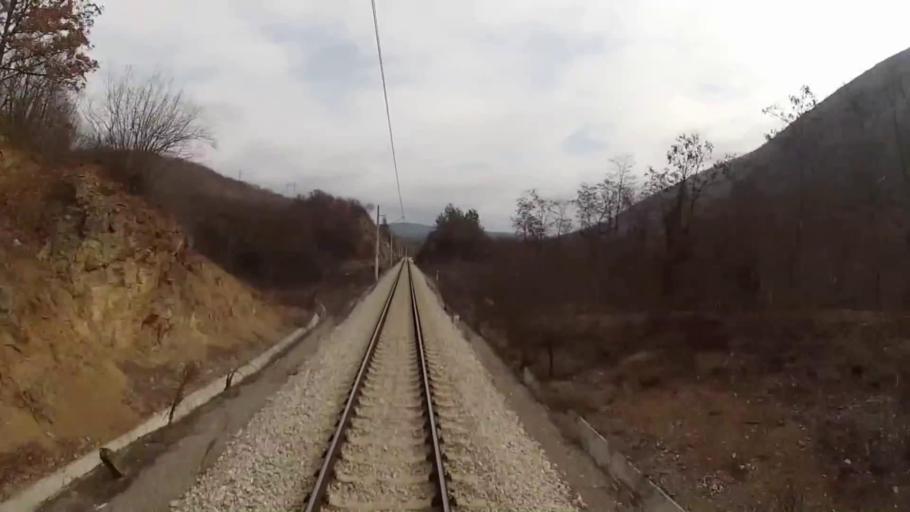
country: BG
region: Sofiya
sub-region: Obshtina Mirkovo
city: Mirkovo
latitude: 42.6900
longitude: 23.8462
